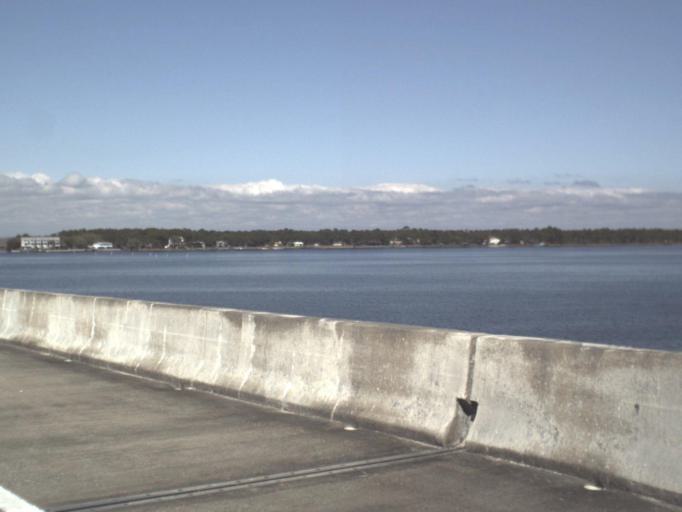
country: US
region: Florida
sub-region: Wakulla County
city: Crawfordville
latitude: 29.9692
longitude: -84.3839
